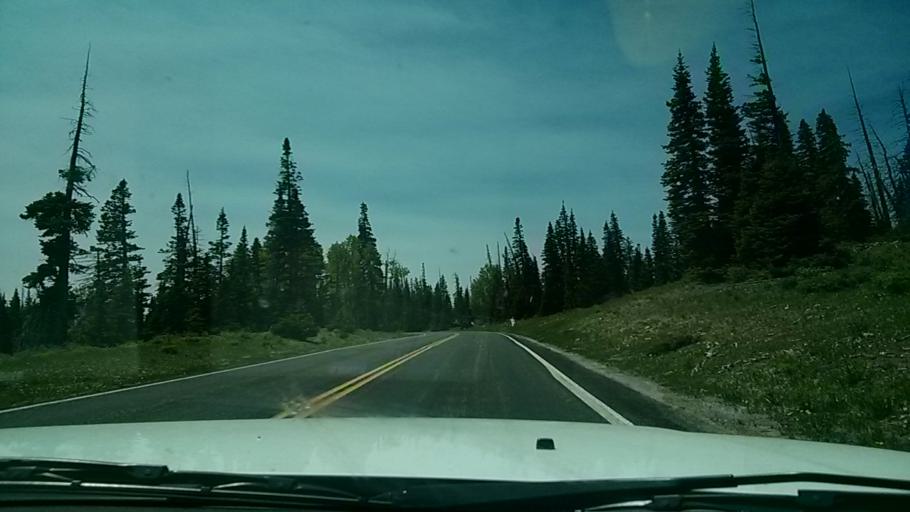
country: US
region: Utah
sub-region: Iron County
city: Parowan
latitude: 37.6206
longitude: -112.8282
